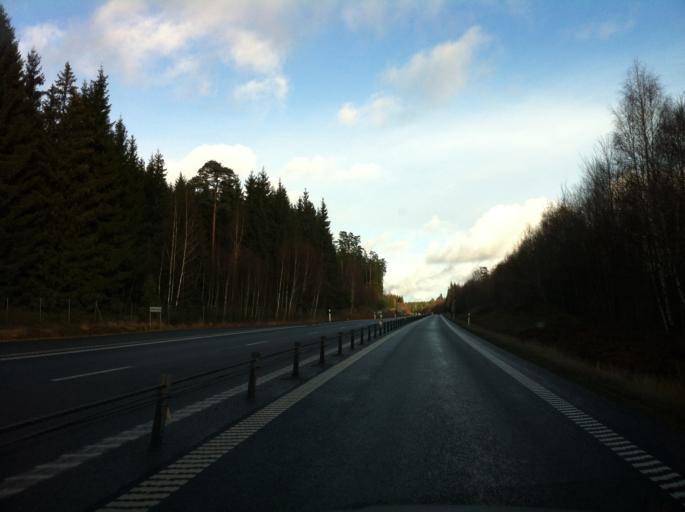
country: SE
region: Skane
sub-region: Osby Kommun
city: Osby
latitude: 56.4062
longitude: 14.0422
